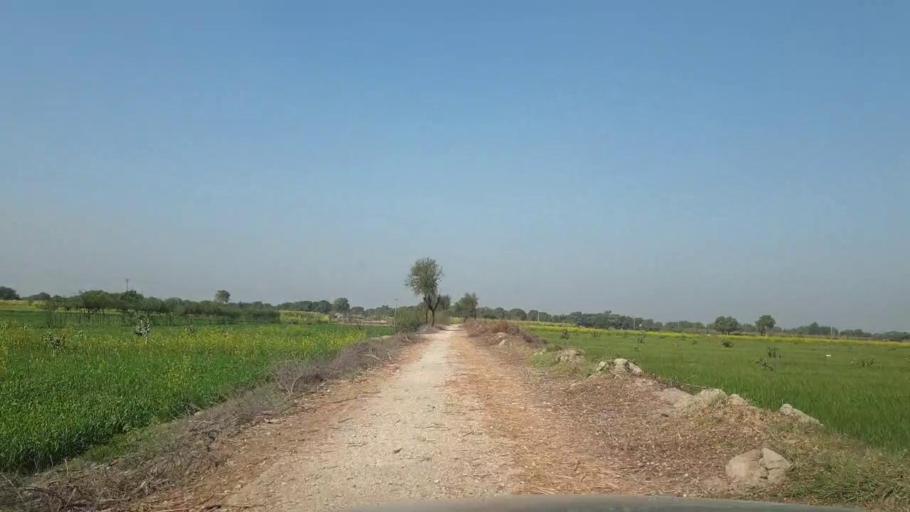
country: PK
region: Sindh
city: Tando Allahyar
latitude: 25.5858
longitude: 68.6510
